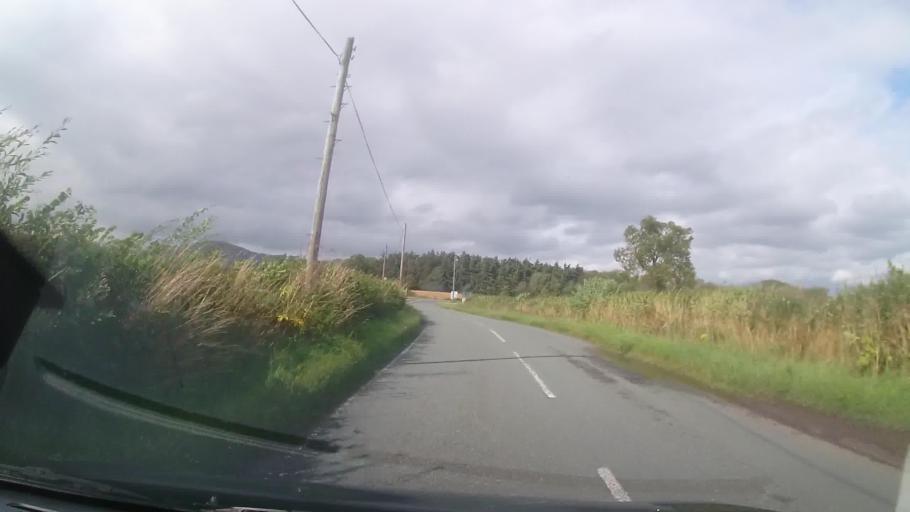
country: GB
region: England
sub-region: Shropshire
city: Lydham
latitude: 52.5042
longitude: -2.9661
